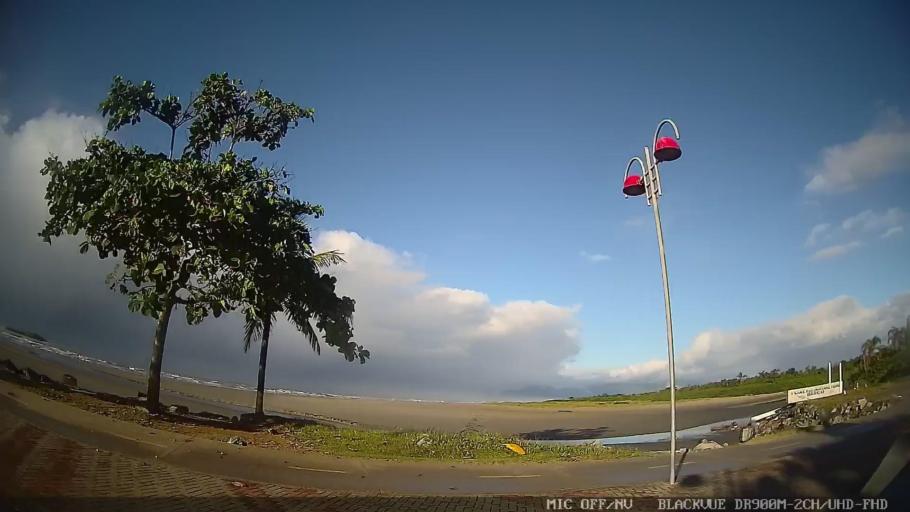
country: BR
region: Sao Paulo
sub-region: Itanhaem
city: Itanhaem
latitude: -24.2480
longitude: -46.8919
